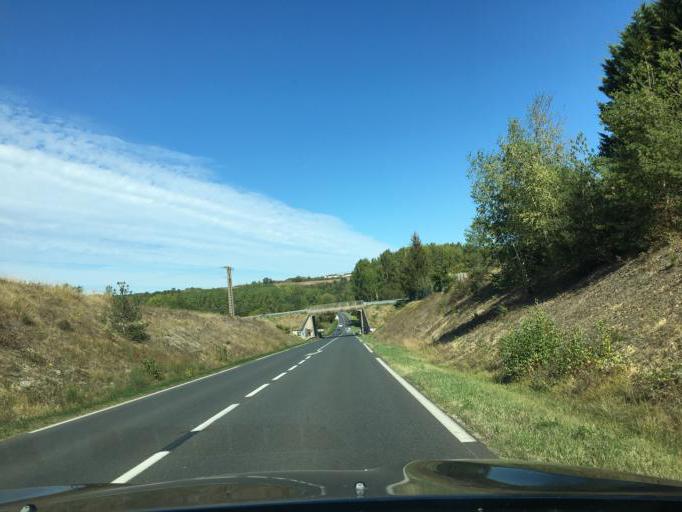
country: FR
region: Centre
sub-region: Departement d'Indre-et-Loire
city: Azay-le-Rideau
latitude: 47.2549
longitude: 0.4551
